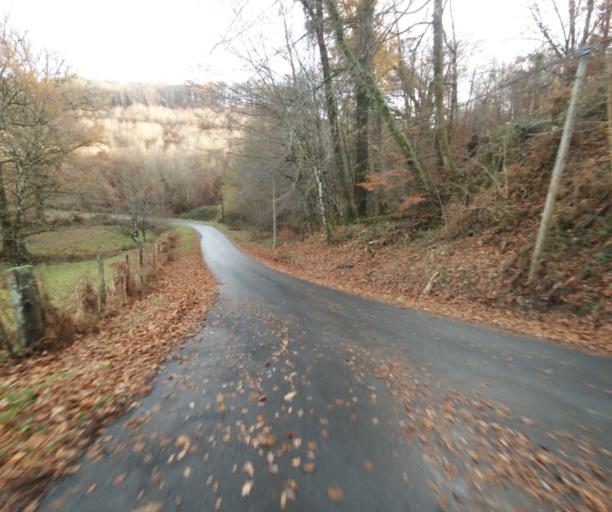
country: FR
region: Limousin
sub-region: Departement de la Correze
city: Cornil
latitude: 45.1961
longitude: 1.6961
